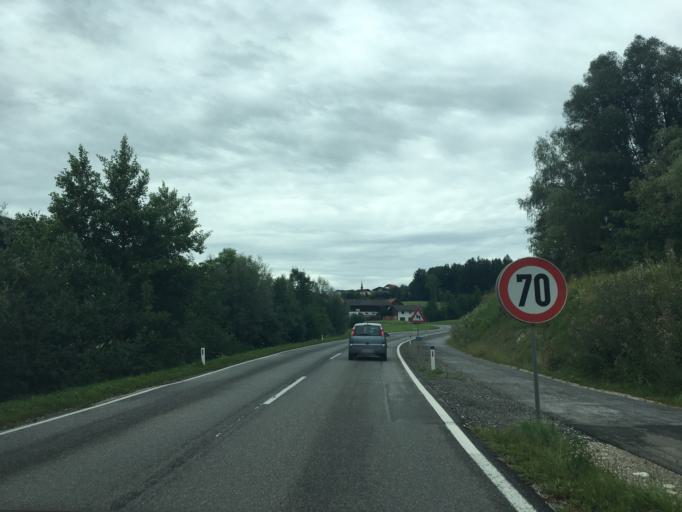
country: AT
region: Salzburg
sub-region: Politischer Bezirk Salzburg-Umgebung
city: Dorfbeuern
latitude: 48.0657
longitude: 12.9885
